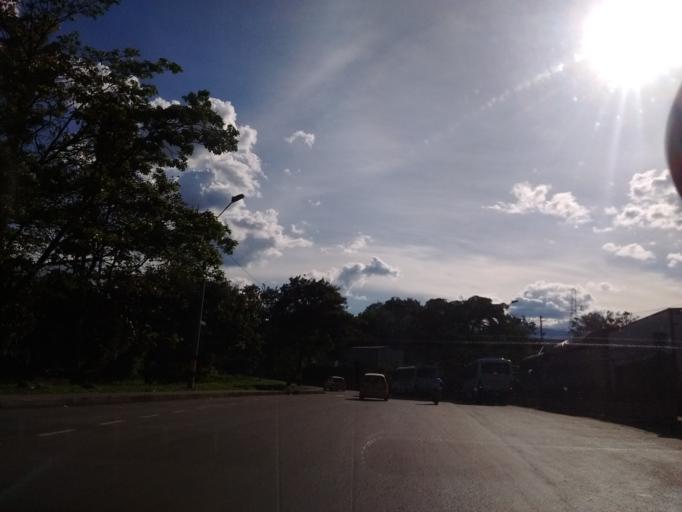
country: CO
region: Antioquia
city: Medellin
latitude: 6.2757
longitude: -75.5709
